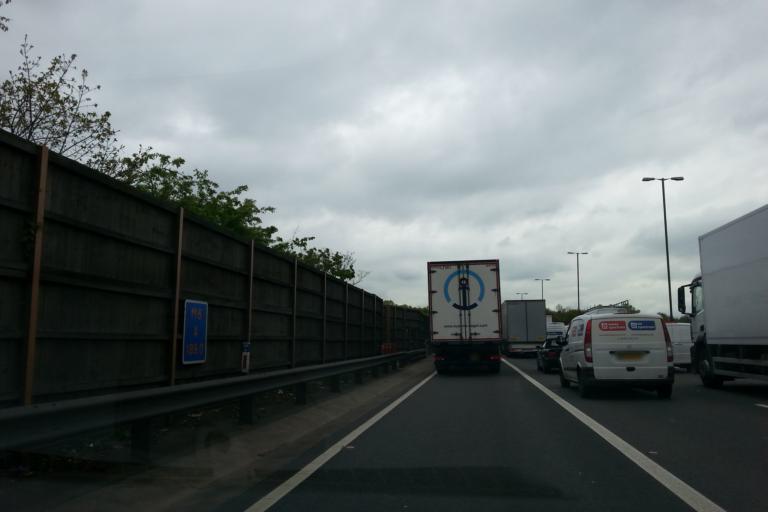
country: GB
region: England
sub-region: City and Borough of Birmingham
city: Hockley
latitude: 52.5460
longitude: -1.9176
